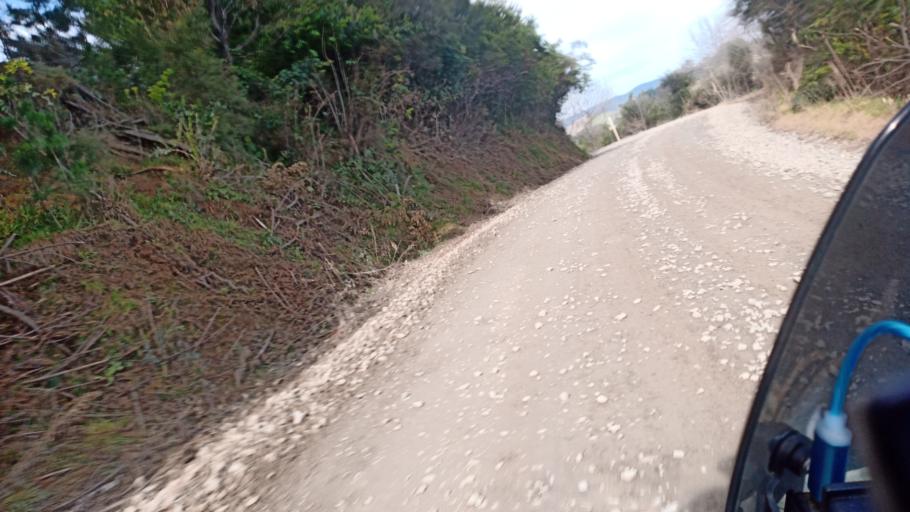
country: NZ
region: Gisborne
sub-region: Gisborne District
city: Gisborne
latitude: -38.1293
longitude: 178.1777
